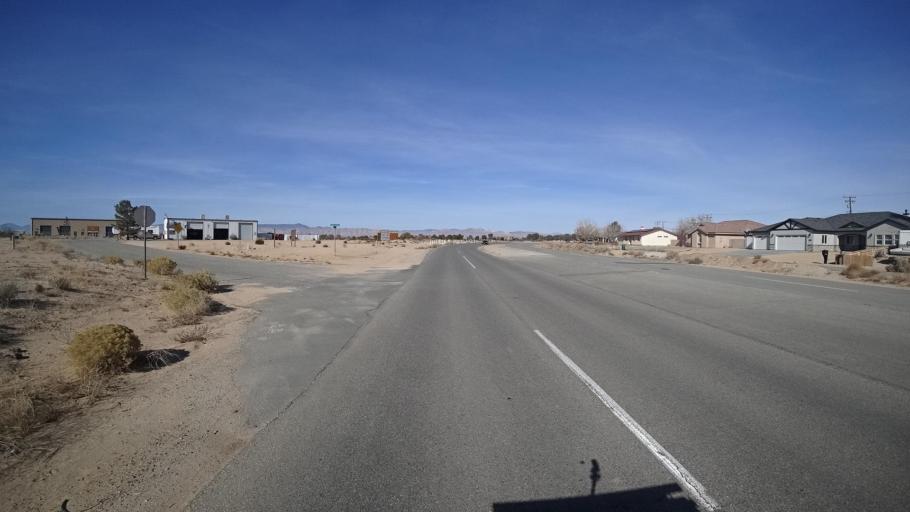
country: US
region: California
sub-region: Kern County
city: California City
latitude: 35.1198
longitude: -117.9398
